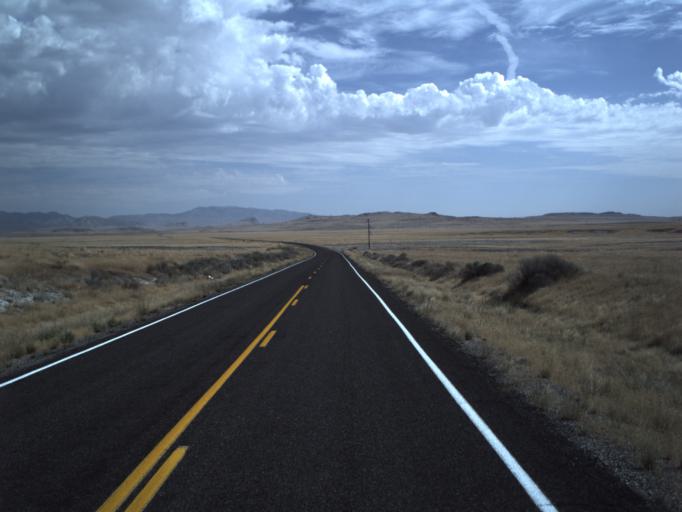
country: US
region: Utah
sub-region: Tooele County
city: Wendover
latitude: 41.3784
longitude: -114.0018
